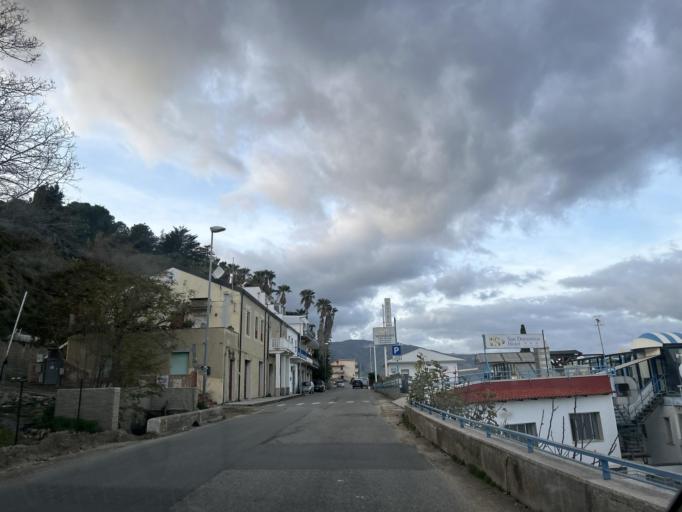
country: IT
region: Calabria
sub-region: Provincia di Catanzaro
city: Soverato Superiore
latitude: 38.6945
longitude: 16.5441
